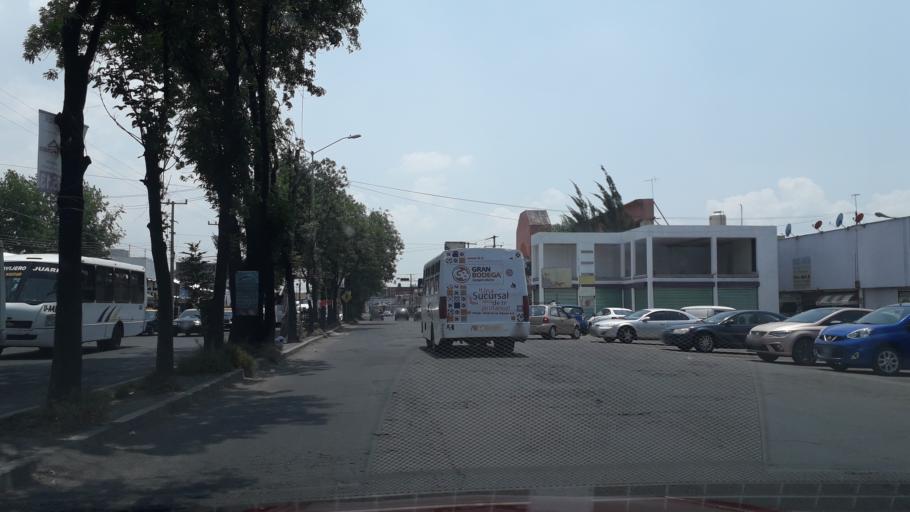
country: MX
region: Puebla
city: Puebla
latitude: 19.0502
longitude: -98.1670
